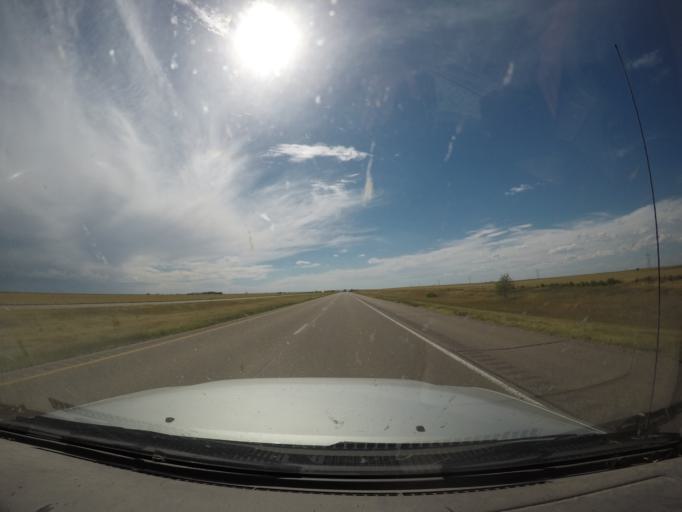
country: US
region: Nebraska
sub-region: Deuel County
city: Chappell
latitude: 41.0497
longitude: -102.3643
